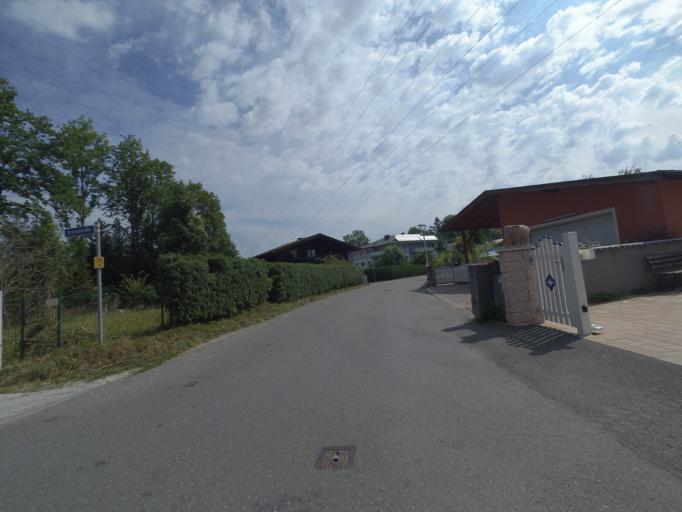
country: DE
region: Bavaria
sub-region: Upper Bavaria
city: Ainring
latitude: 47.8113
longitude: 12.9766
